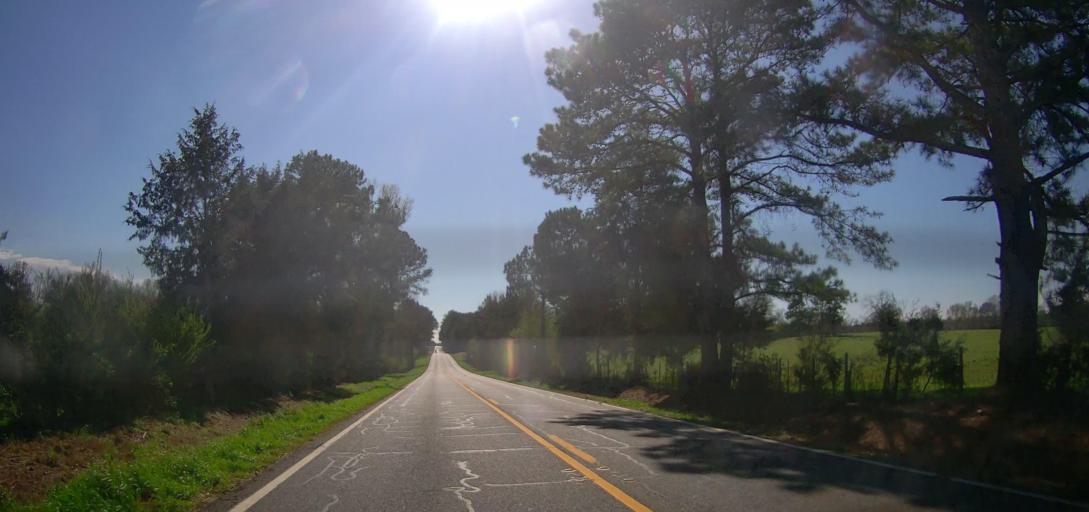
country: US
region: Georgia
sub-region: Butts County
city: Indian Springs
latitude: 33.1995
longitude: -83.9389
